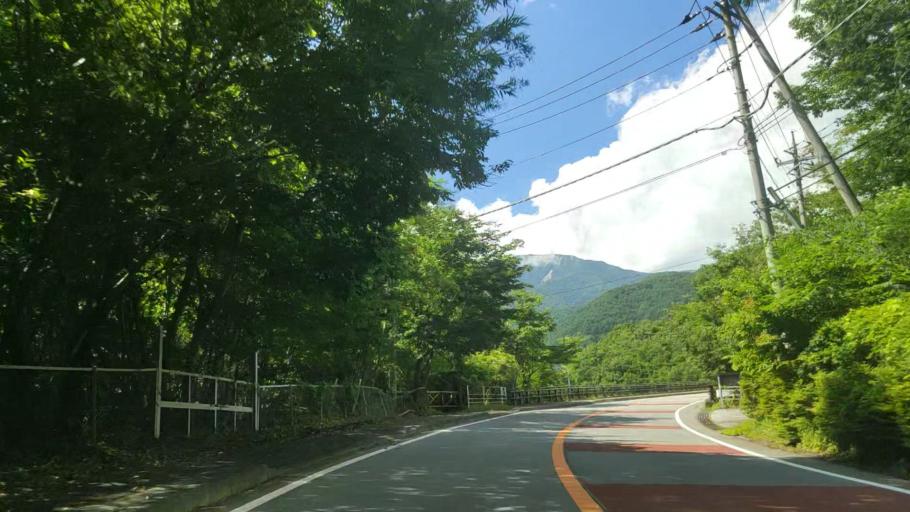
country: JP
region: Yamanashi
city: Enzan
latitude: 35.8569
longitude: 138.7569
